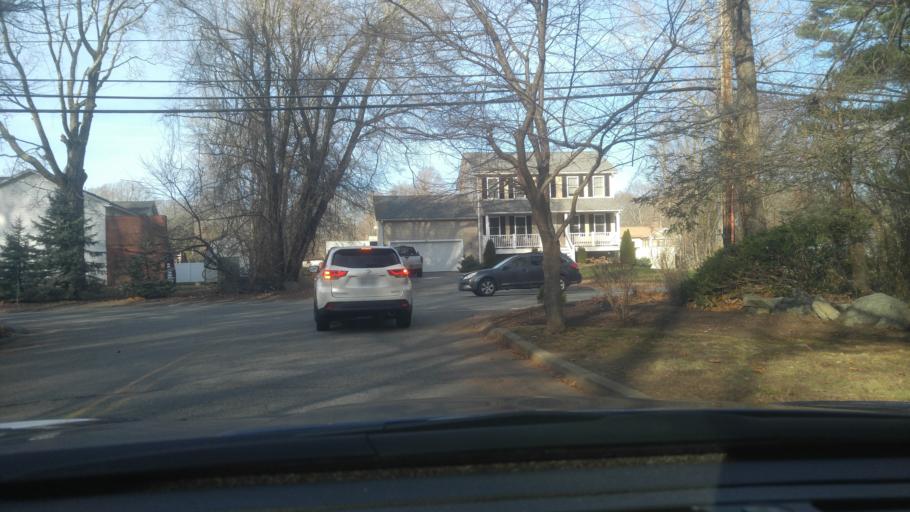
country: US
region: Rhode Island
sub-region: Kent County
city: East Greenwich
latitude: 41.6849
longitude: -71.4716
